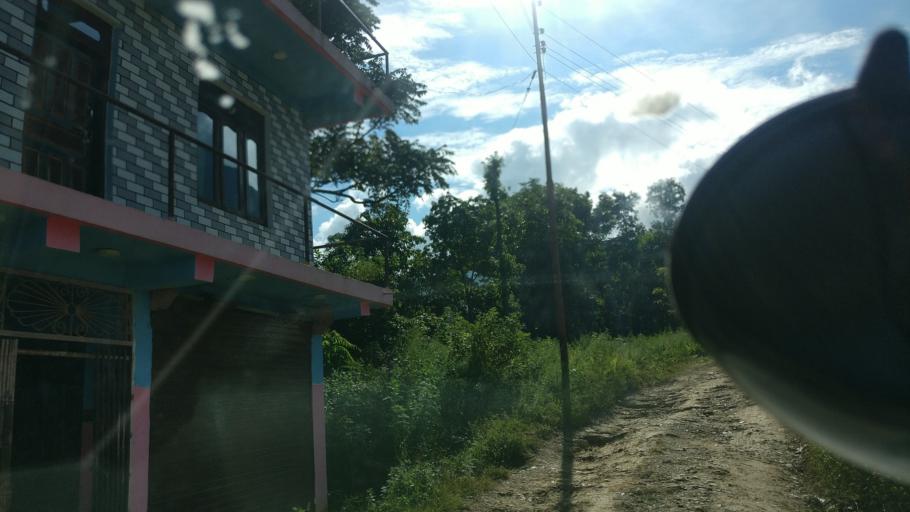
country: NP
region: Western Region
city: Baglung
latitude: 28.1353
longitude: 83.6562
